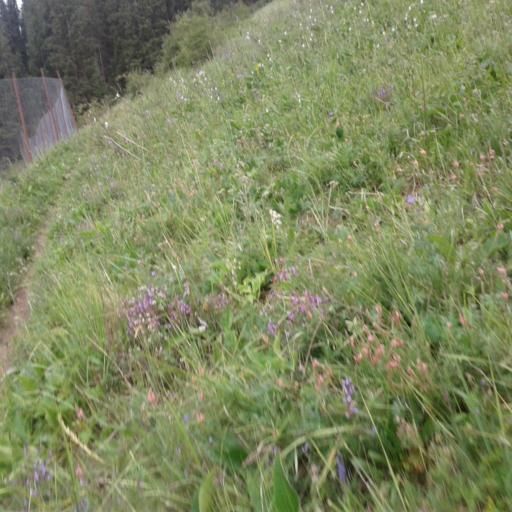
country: KG
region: Naryn
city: Naryn
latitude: 41.4559
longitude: 76.4524
